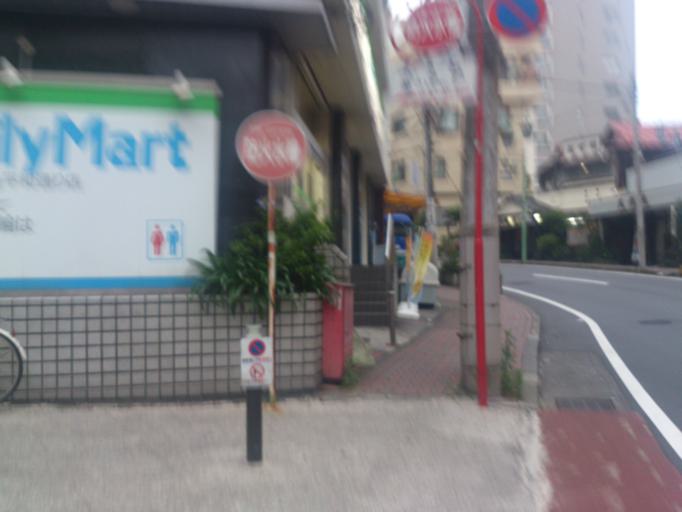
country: JP
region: Shizuoka
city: Atami
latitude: 35.1017
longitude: 139.0763
